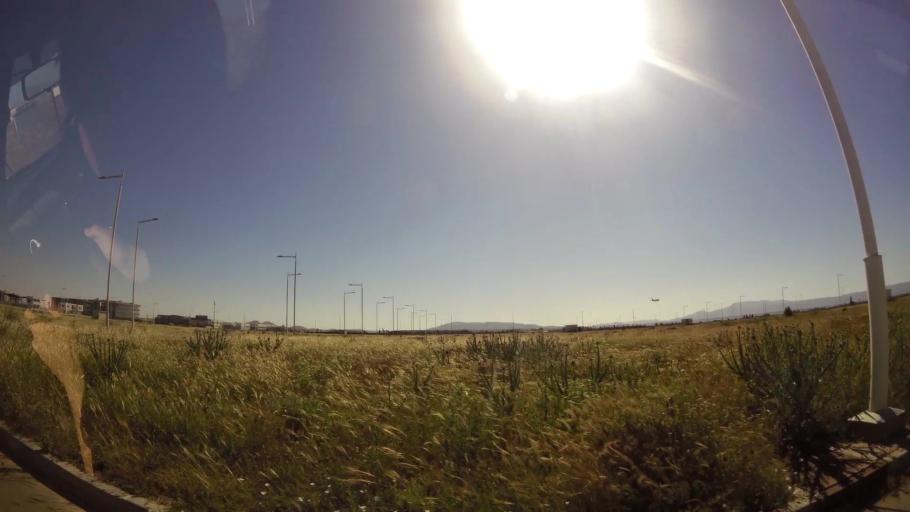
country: MA
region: Oriental
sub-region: Oujda-Angad
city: Oujda
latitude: 34.7733
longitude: -1.9353
